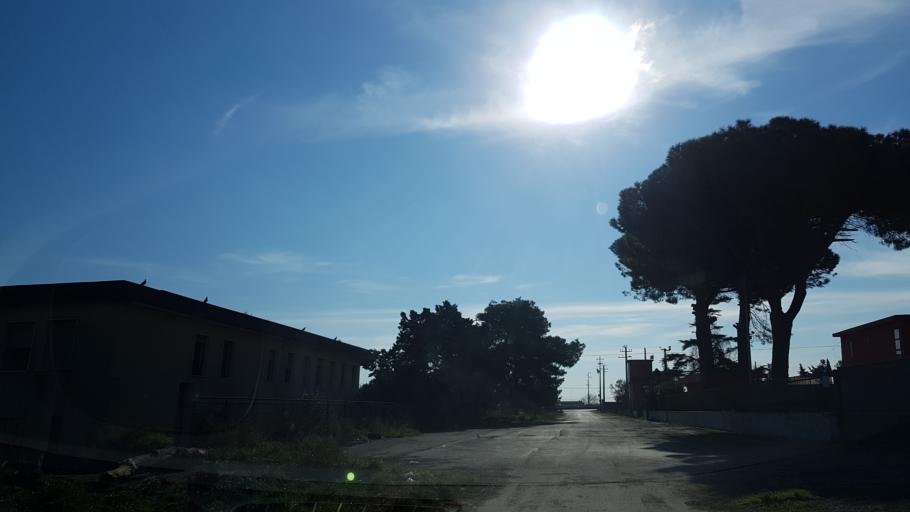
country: IT
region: Apulia
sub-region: Provincia di Brindisi
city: Brindisi
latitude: 40.6095
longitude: 17.8870
